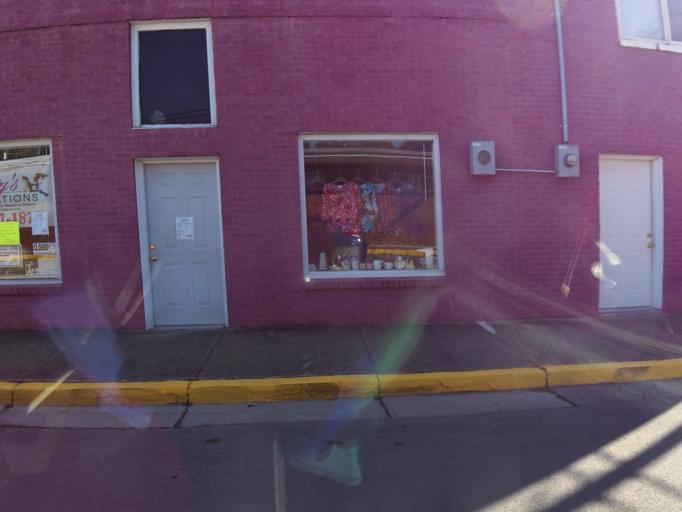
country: US
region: Kentucky
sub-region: Whitley County
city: Williamsburg
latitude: 36.7417
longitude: -84.1600
